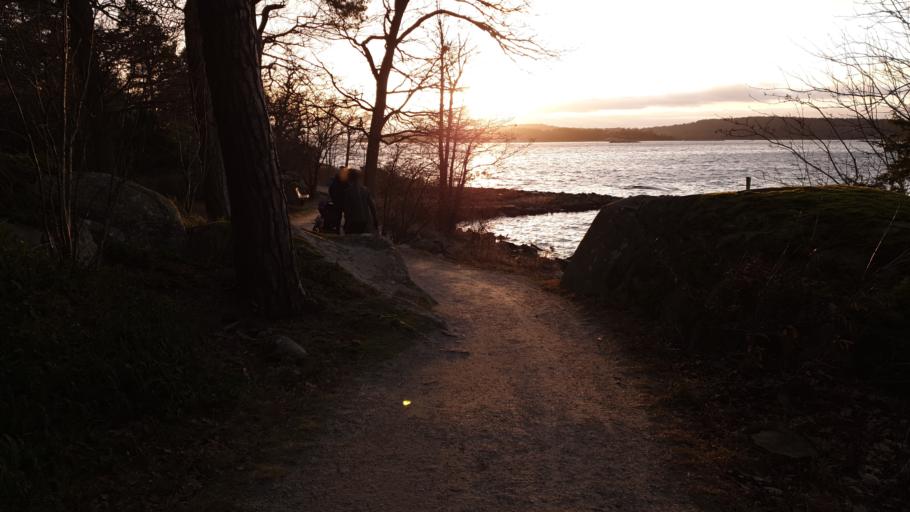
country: SE
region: Blekinge
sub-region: Karlshamns Kommun
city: Karlshamn
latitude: 56.1599
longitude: 14.8785
